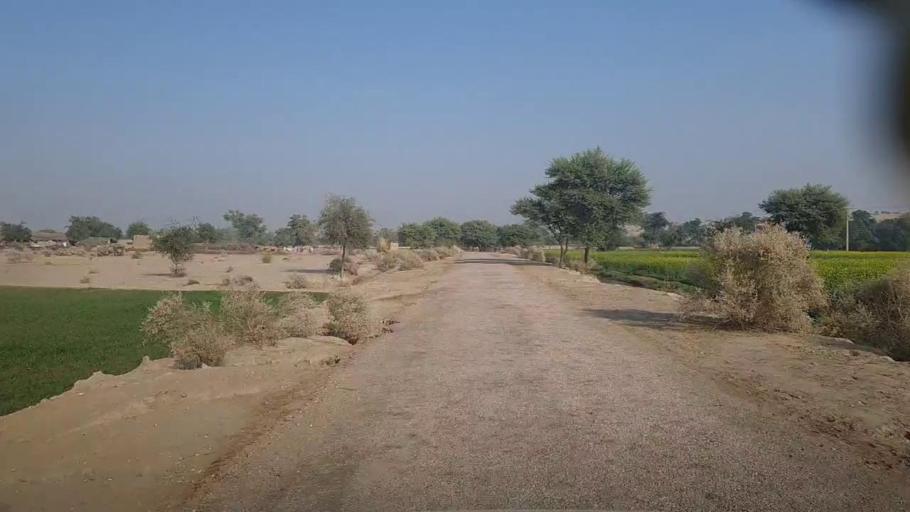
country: PK
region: Sindh
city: Kandiari
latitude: 26.7679
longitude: 68.5086
